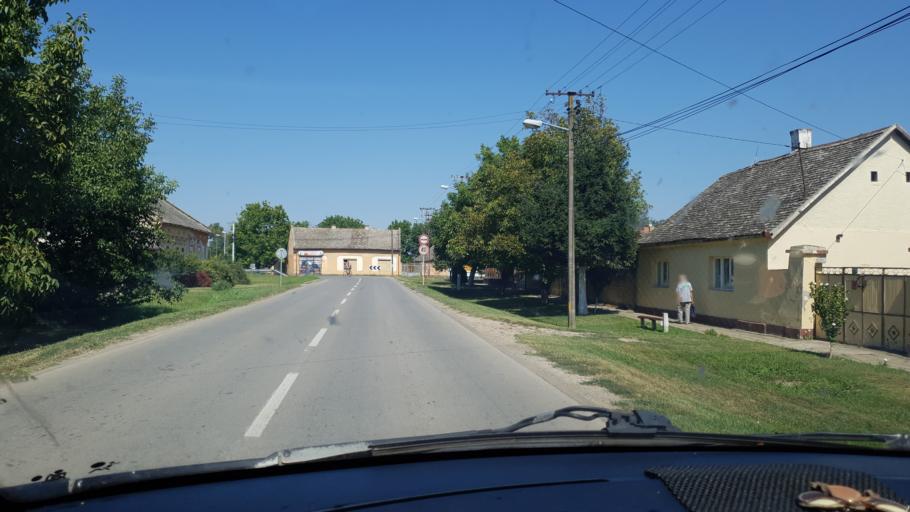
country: RS
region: Autonomna Pokrajina Vojvodina
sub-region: Juznobacki Okrug
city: Kovilj
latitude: 45.2330
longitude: 20.0261
